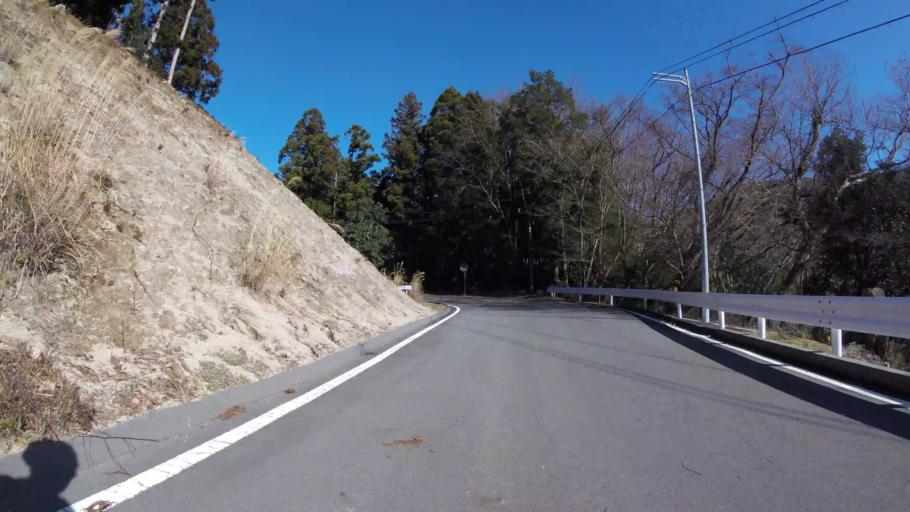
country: JP
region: Shizuoka
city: Ito
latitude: 34.8948
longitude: 138.9510
